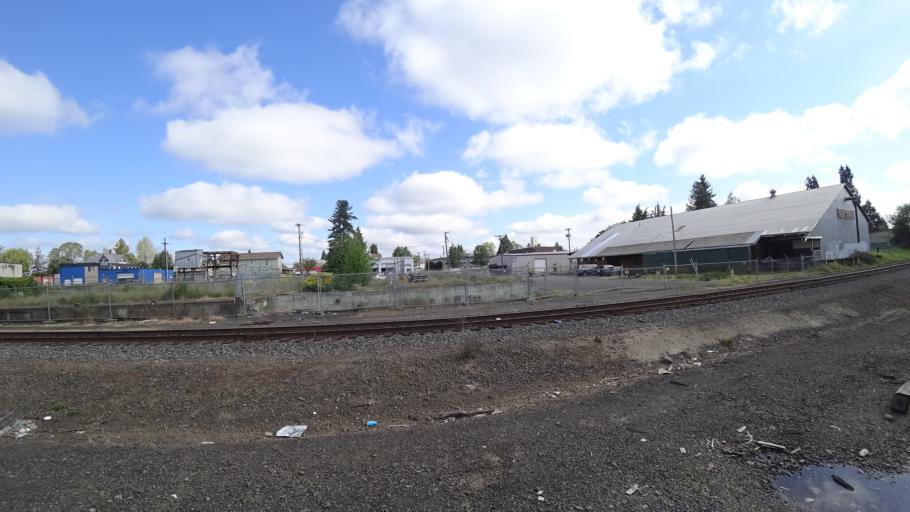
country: US
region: Oregon
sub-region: Washington County
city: Hillsboro
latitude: 45.5162
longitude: -122.9885
